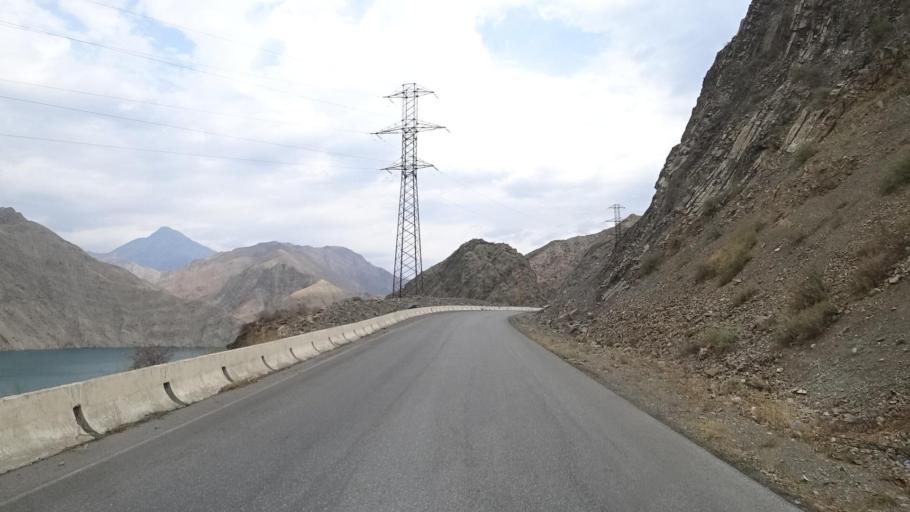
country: KG
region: Jalal-Abad
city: Tash-Kumyr
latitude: 41.5022
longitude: 72.3859
